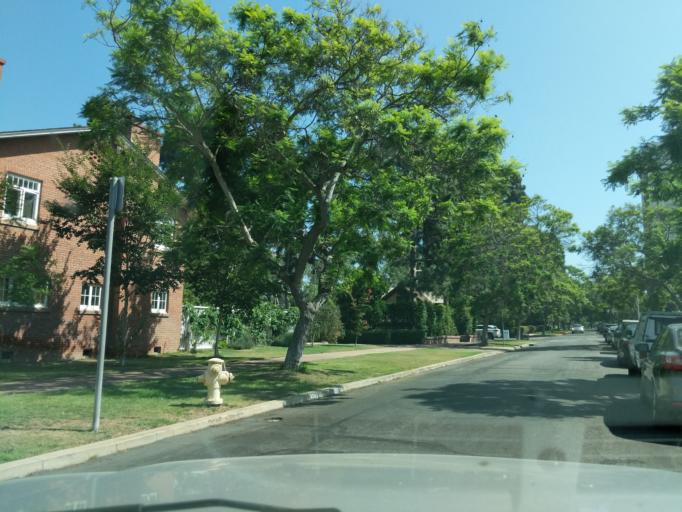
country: US
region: California
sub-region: San Diego County
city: San Diego
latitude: 32.7429
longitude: -117.1584
